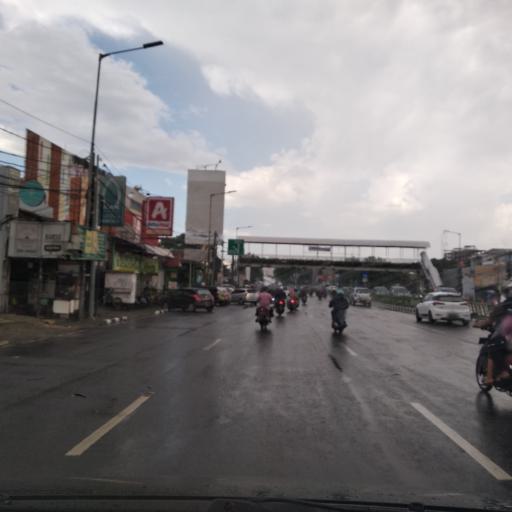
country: ID
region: Jakarta Raya
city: Jakarta
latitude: -6.2251
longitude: 106.8620
